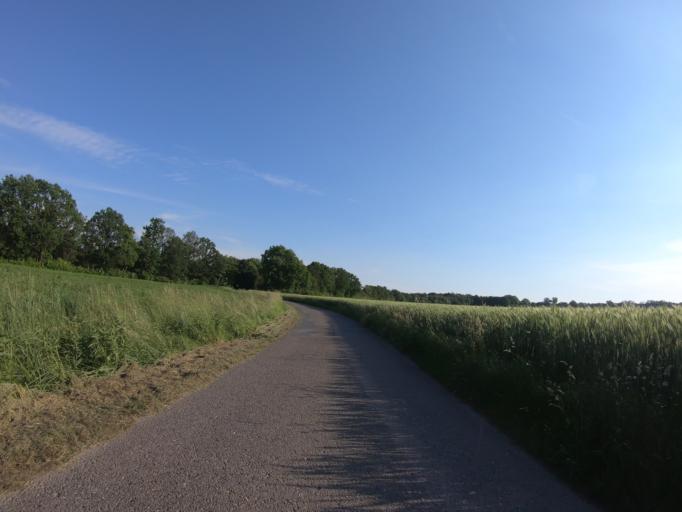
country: DE
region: Lower Saxony
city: Meine
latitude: 52.3598
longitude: 10.5530
